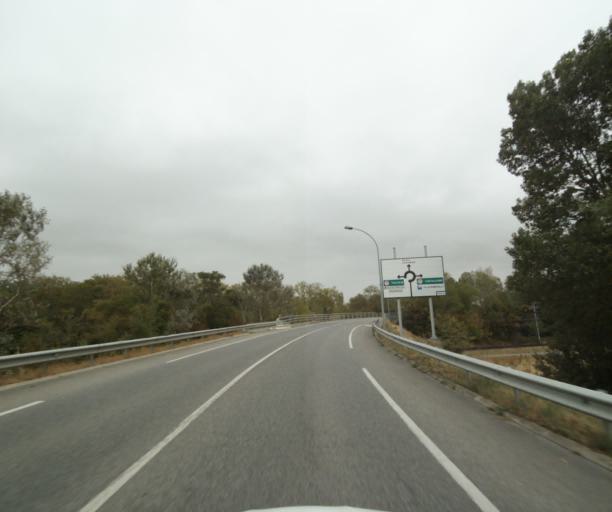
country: FR
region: Midi-Pyrenees
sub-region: Departement de la Haute-Garonne
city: Villefranche-de-Lauragais
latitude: 43.4058
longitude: 1.7067
